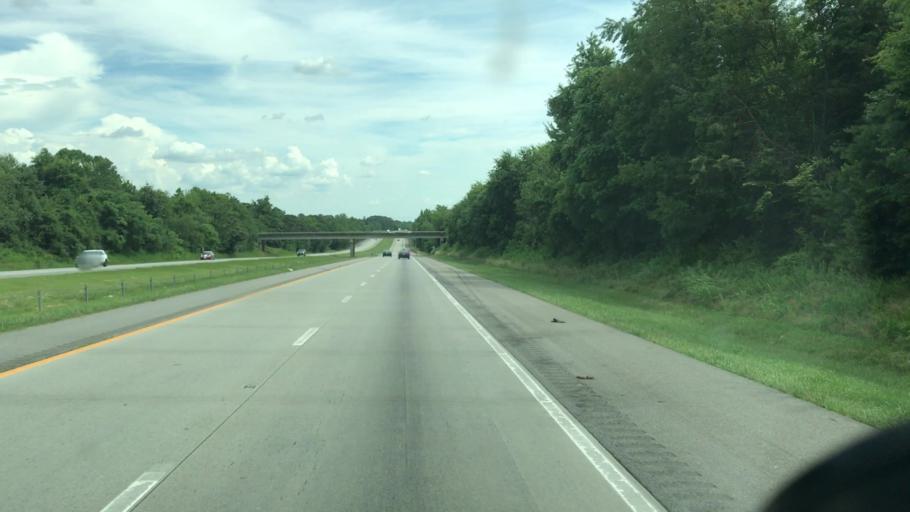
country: US
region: North Carolina
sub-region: Yadkin County
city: Jonesville
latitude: 36.1592
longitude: -80.8082
